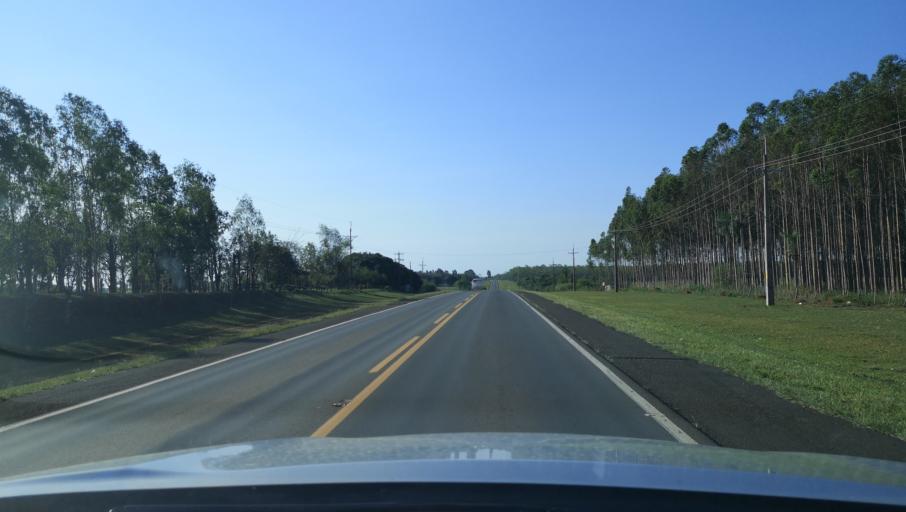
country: PY
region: Misiones
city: Santa Maria
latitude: -26.7734
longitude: -57.0299
